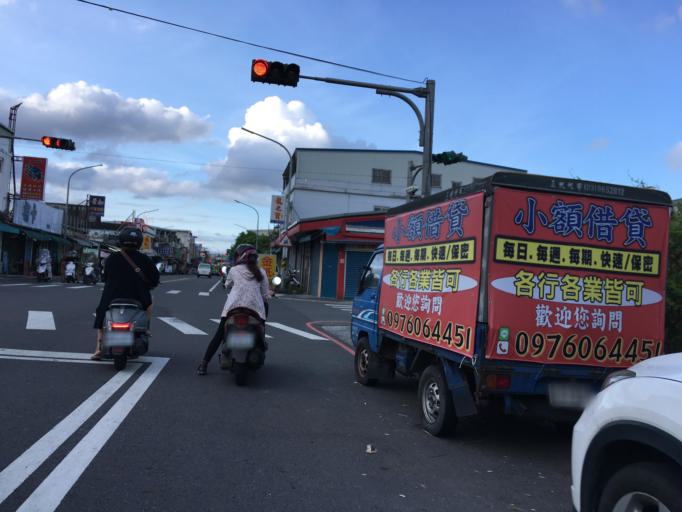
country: TW
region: Taiwan
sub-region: Yilan
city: Yilan
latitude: 24.6645
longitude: 121.7672
